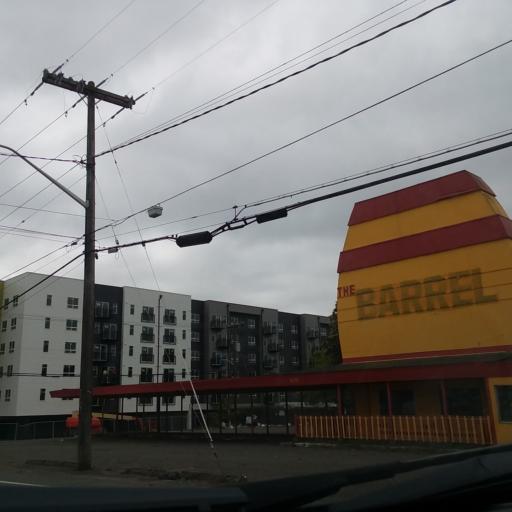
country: US
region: Washington
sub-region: King County
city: Boulevard Park
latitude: 47.5036
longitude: -122.3337
